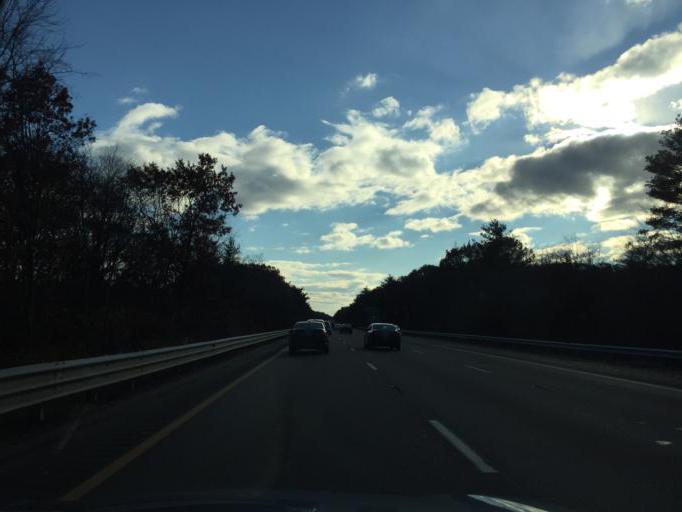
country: US
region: Massachusetts
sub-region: Norfolk County
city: Foxborough
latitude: 42.0743
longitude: -71.2251
